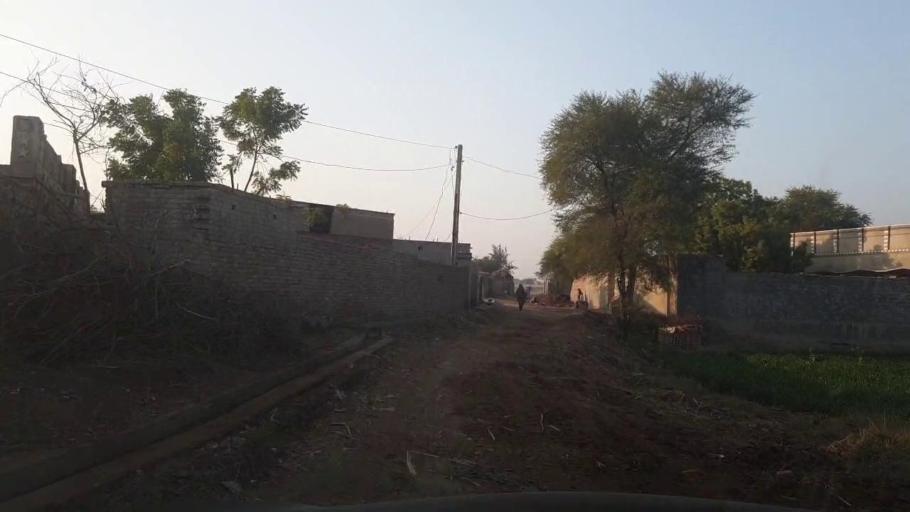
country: PK
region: Sindh
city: Ubauro
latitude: 28.3205
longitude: 69.7757
